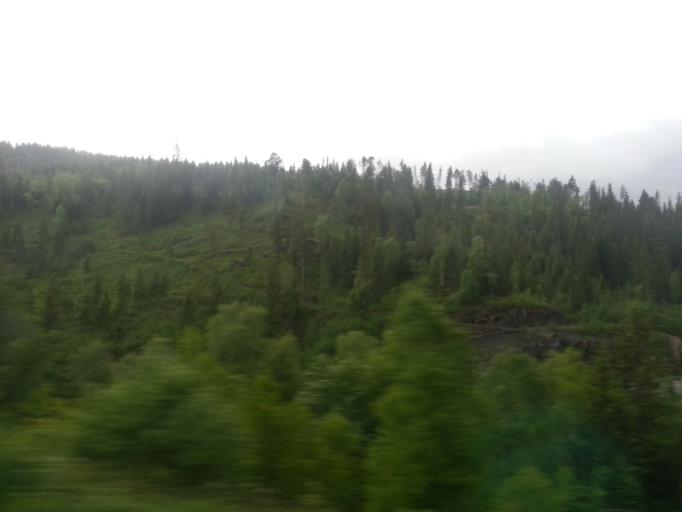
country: NO
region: Sor-Trondelag
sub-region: Midtre Gauldal
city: Storen
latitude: 62.9294
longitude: 10.1671
